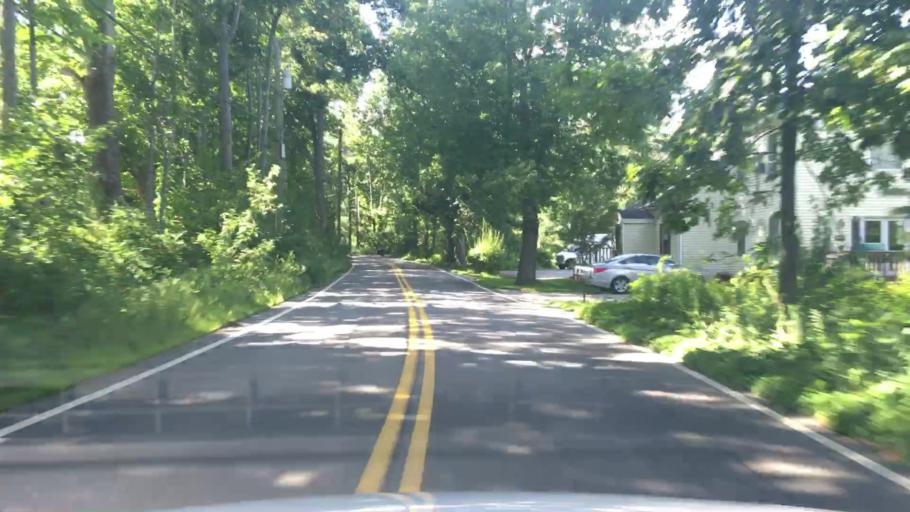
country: US
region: New Hampshire
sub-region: Strafford County
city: Dover
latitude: 43.1810
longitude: -70.8393
